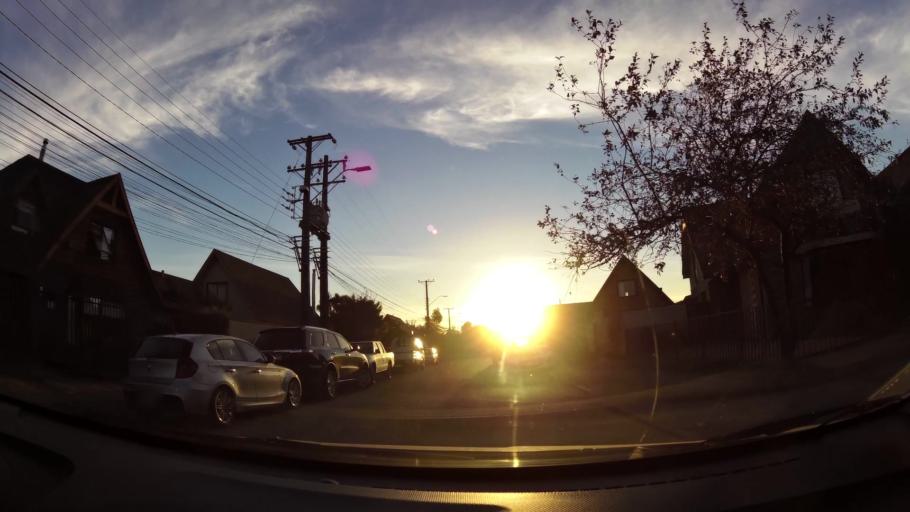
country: CL
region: Biobio
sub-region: Provincia de Concepcion
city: Concepcion
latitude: -36.8401
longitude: -73.0976
